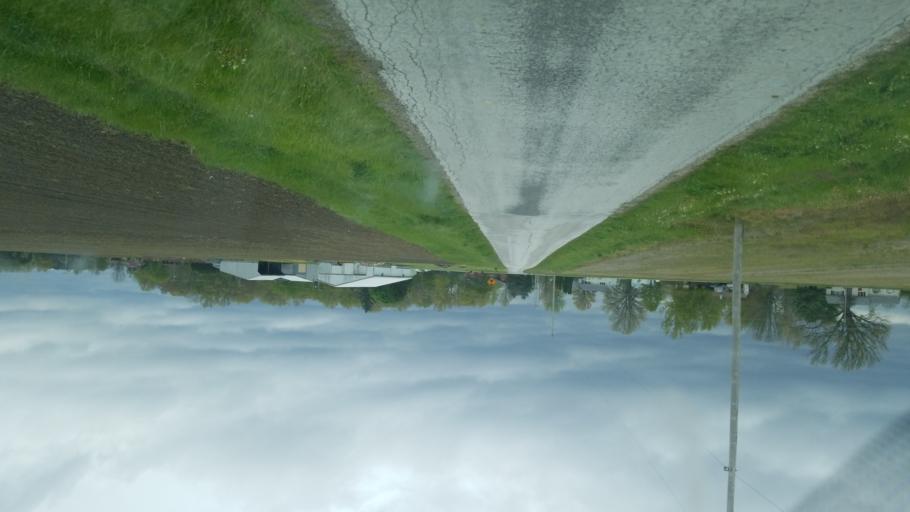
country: US
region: Ohio
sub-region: Marion County
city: Prospect
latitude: 40.5158
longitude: -83.2390
